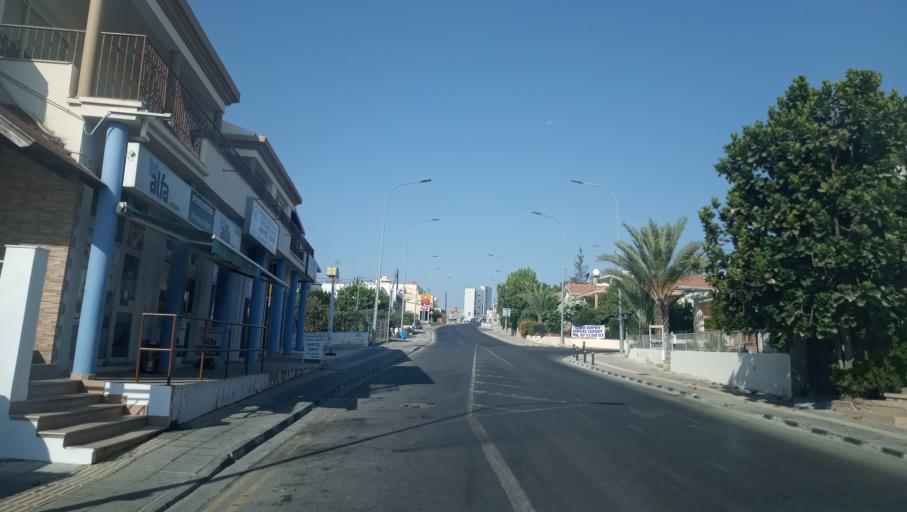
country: CY
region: Lefkosia
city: Geri
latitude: 35.1064
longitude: 33.4214
